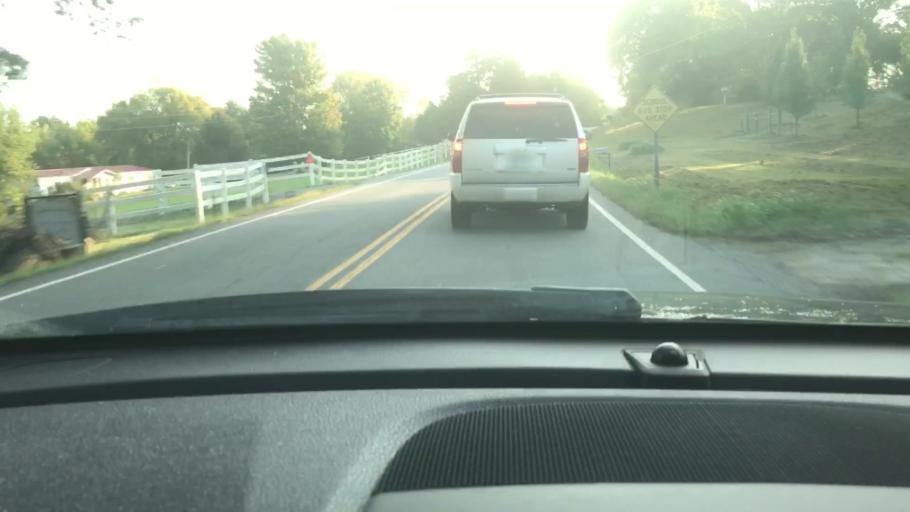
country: US
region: Tennessee
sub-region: Dickson County
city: Charlotte
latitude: 36.2573
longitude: -87.2256
